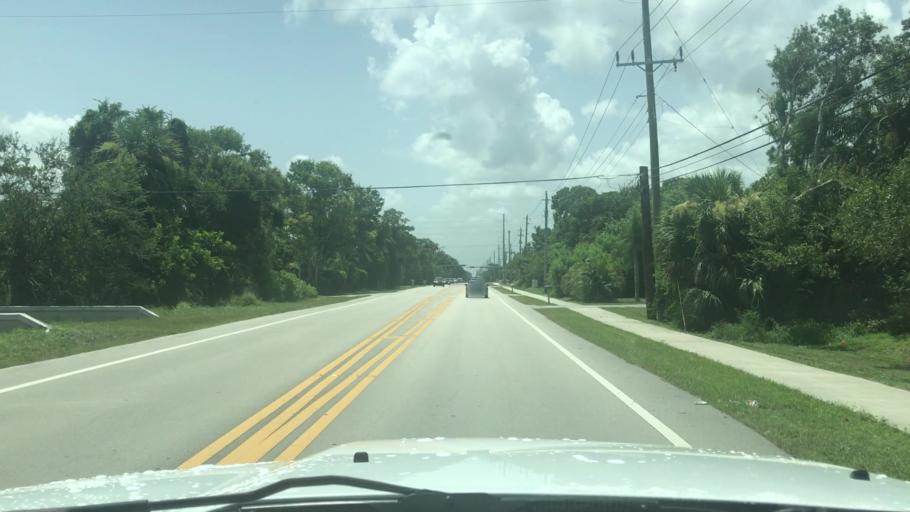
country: US
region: Florida
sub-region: Indian River County
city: Vero Beach South
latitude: 27.6237
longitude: -80.4105
